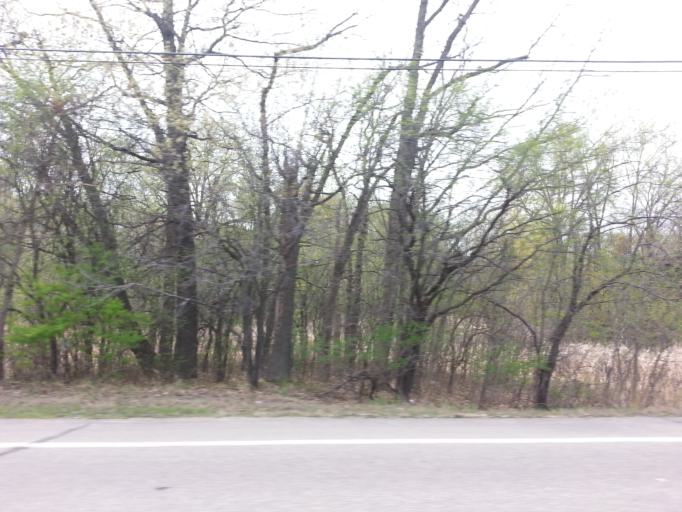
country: US
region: Minnesota
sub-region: Hennepin County
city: Edina
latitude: 44.8441
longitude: -93.3738
